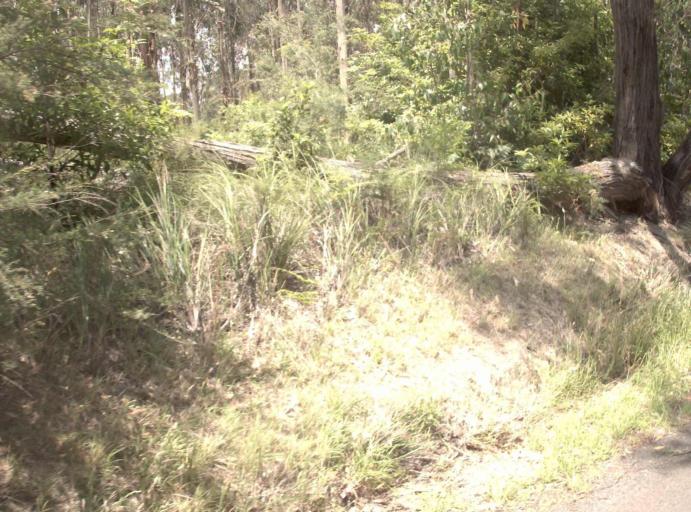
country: AU
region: Victoria
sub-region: Latrobe
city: Traralgon
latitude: -38.3704
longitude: 146.7571
